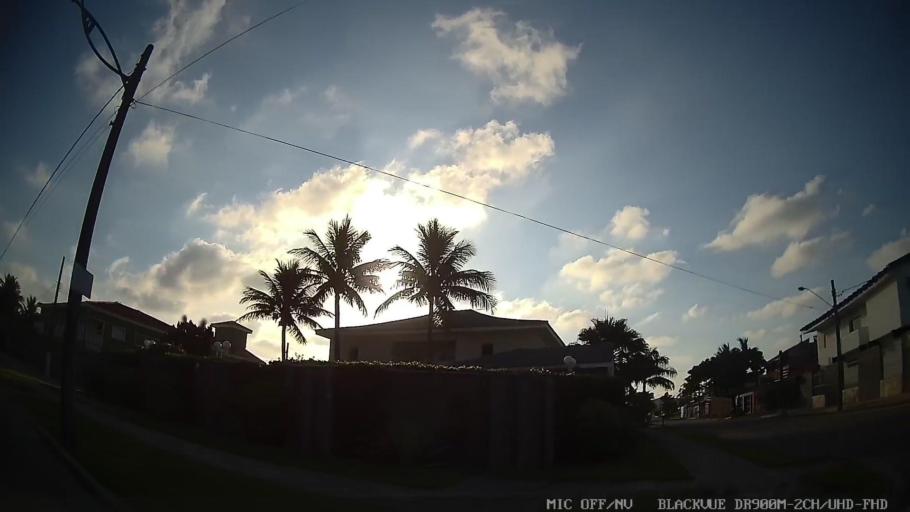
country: BR
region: Sao Paulo
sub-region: Peruibe
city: Peruibe
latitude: -24.2984
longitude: -46.9661
